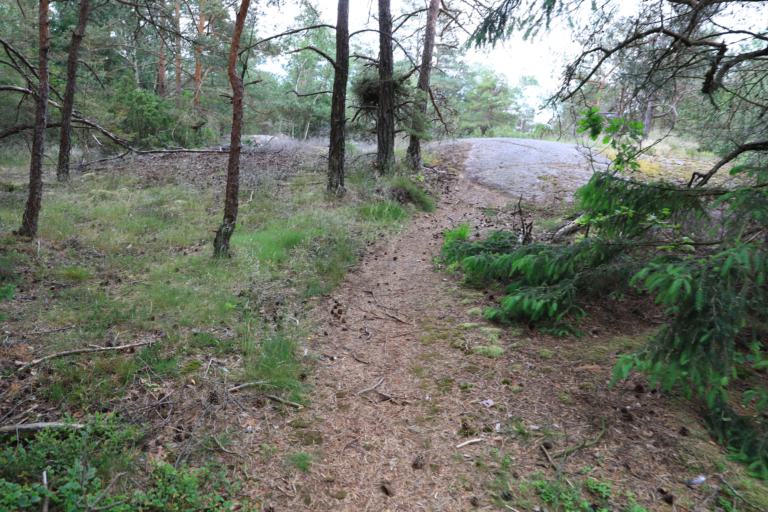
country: SE
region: Halland
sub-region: Varbergs Kommun
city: Varberg
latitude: 57.1697
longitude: 12.2575
